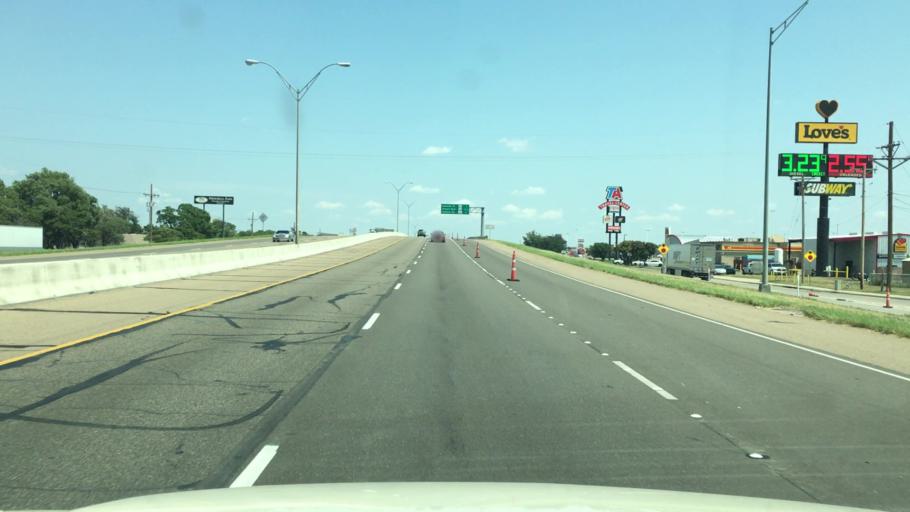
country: US
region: Texas
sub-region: Potter County
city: Amarillo
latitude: 35.1926
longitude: -101.7629
